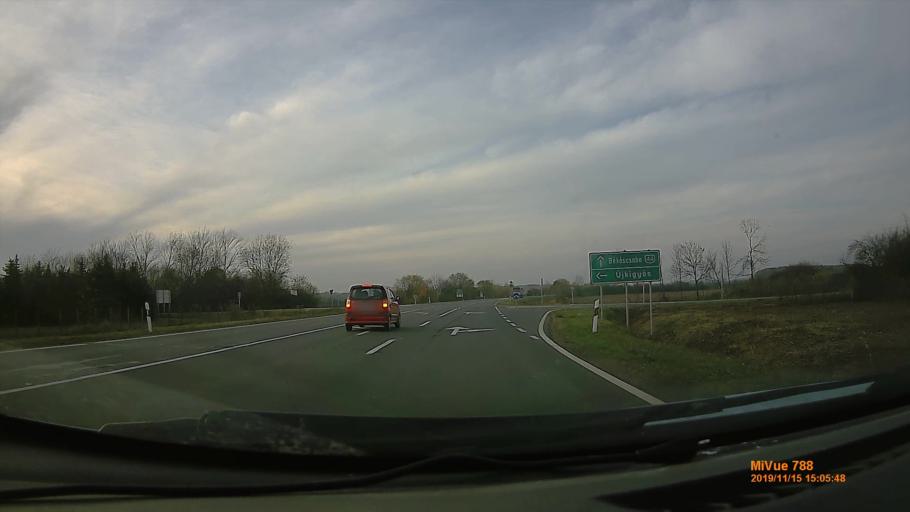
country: HU
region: Bekes
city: Gyula
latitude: 46.6370
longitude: 21.2509
